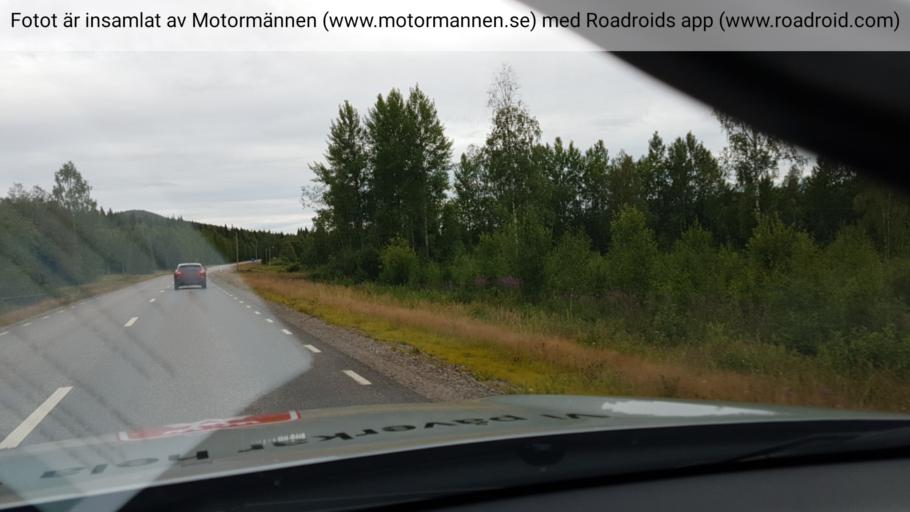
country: SE
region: Norrbotten
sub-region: Overkalix Kommun
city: OEverkalix
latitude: 66.5694
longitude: 22.7603
